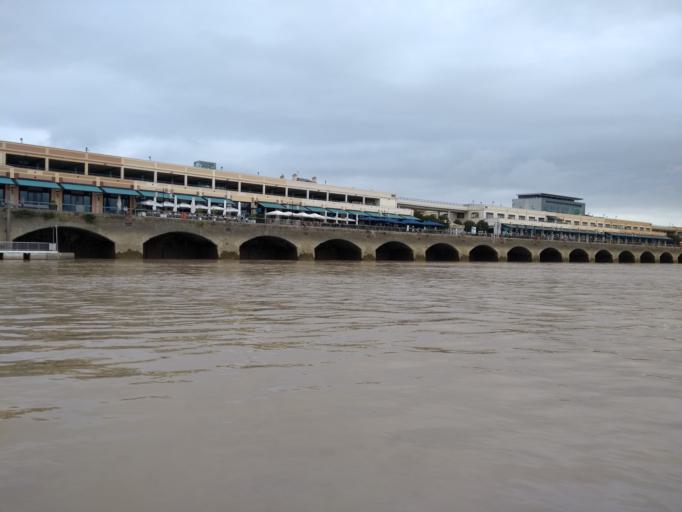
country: FR
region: Aquitaine
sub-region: Departement de la Gironde
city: Bordeaux
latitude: 44.8549
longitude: -0.5621
